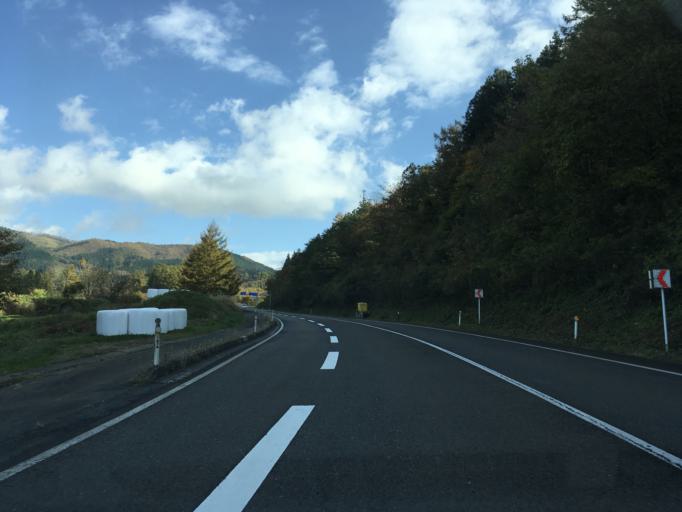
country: JP
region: Iwate
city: Tono
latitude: 39.3629
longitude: 141.4022
